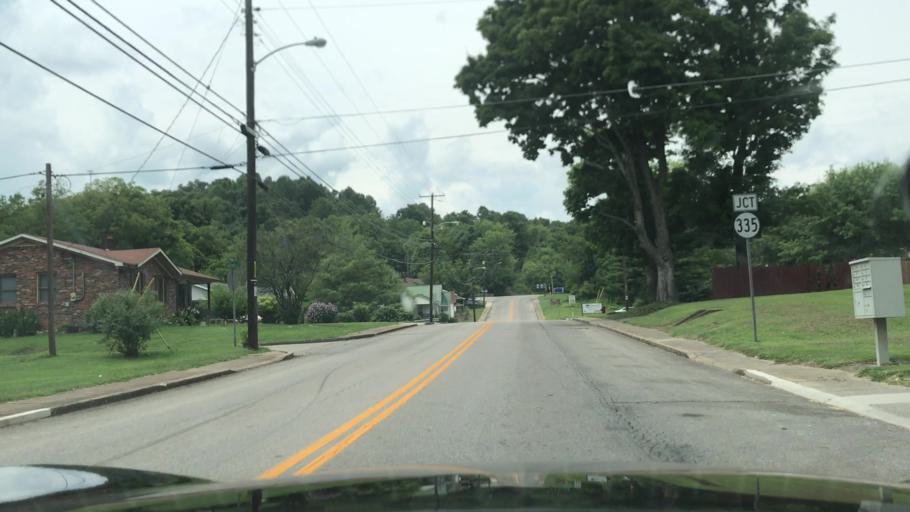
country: US
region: Kentucky
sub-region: Hart County
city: Horse Cave
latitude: 37.1799
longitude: -85.9119
